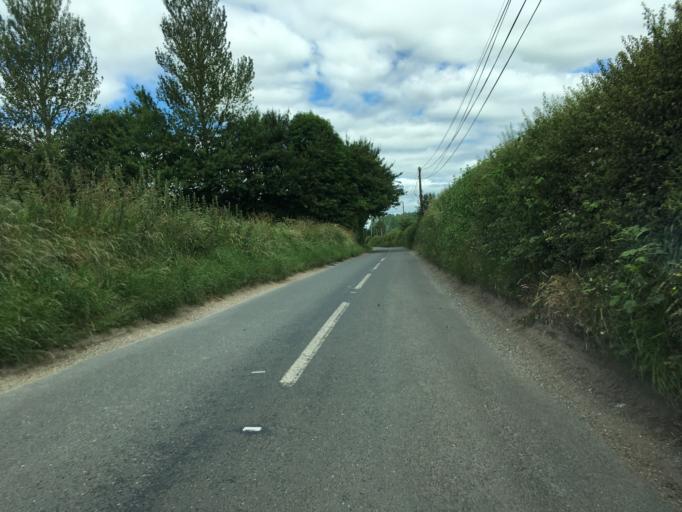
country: GB
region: England
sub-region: West Berkshire
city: Wickham
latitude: 51.4637
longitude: -1.4321
